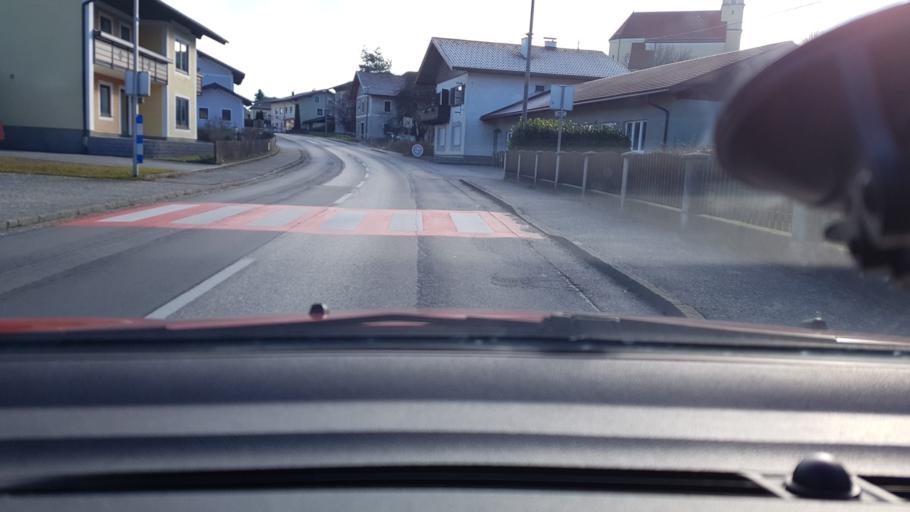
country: AT
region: Salzburg
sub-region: Politischer Bezirk Salzburg-Umgebung
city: Dorfbeuern
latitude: 48.0473
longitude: 12.9880
